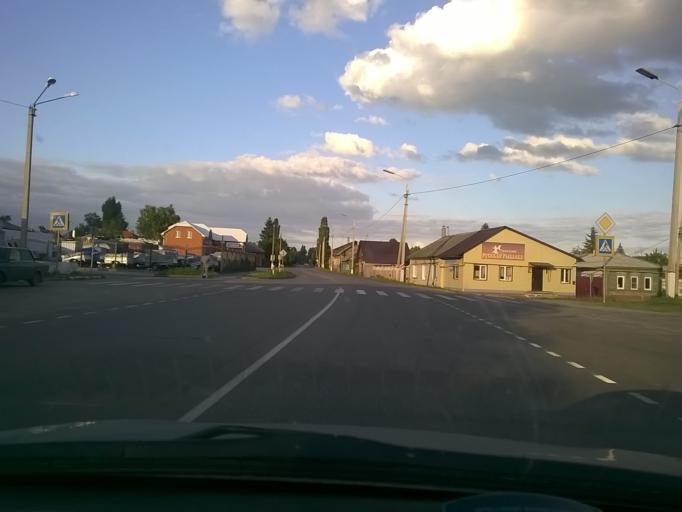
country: RU
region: Voronezj
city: Borisoglebsk
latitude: 51.3752
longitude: 42.0598
